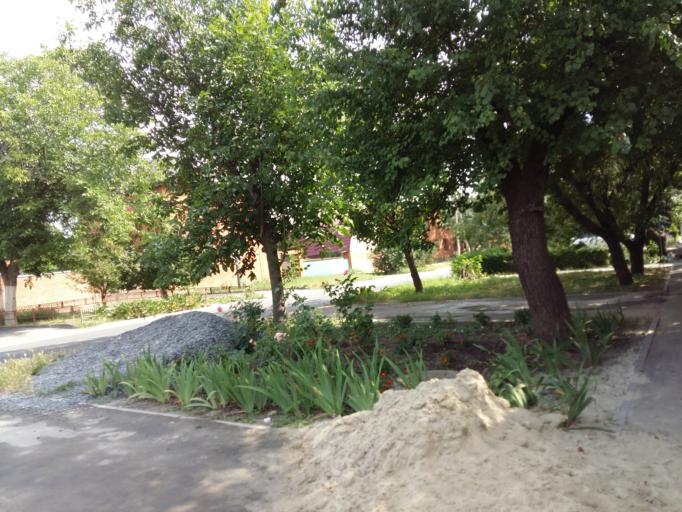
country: RU
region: Rostov
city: Imeni Chkalova
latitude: 47.2812
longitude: 39.7377
